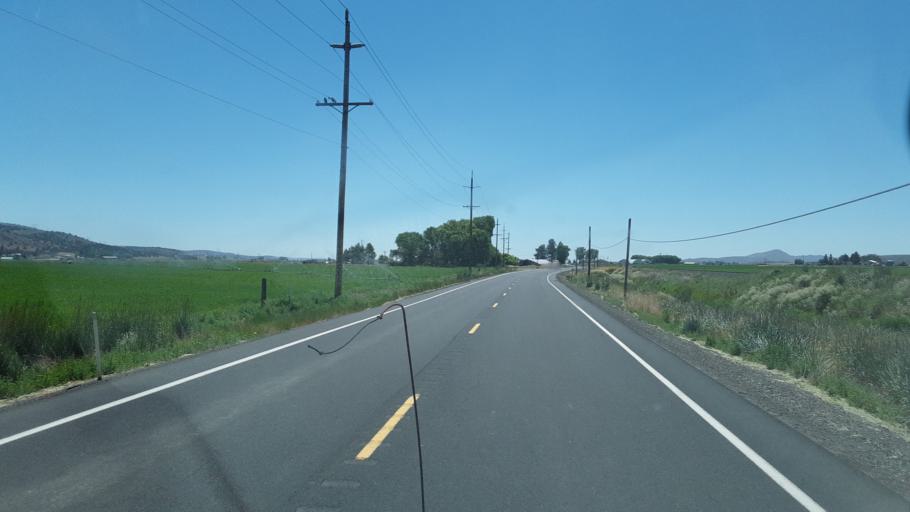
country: US
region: Oregon
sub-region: Klamath County
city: Altamont
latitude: 42.0732
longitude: -121.6692
